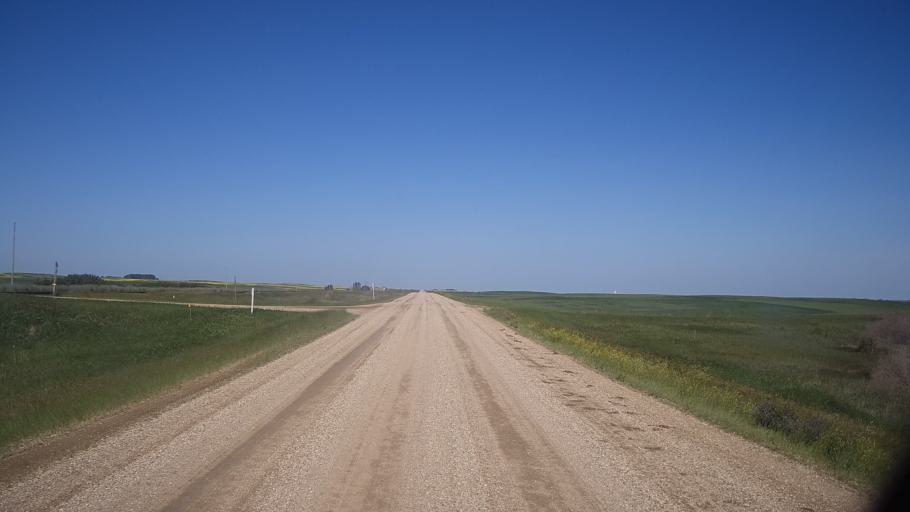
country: CA
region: Saskatchewan
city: Watrous
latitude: 51.8467
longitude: -105.9234
